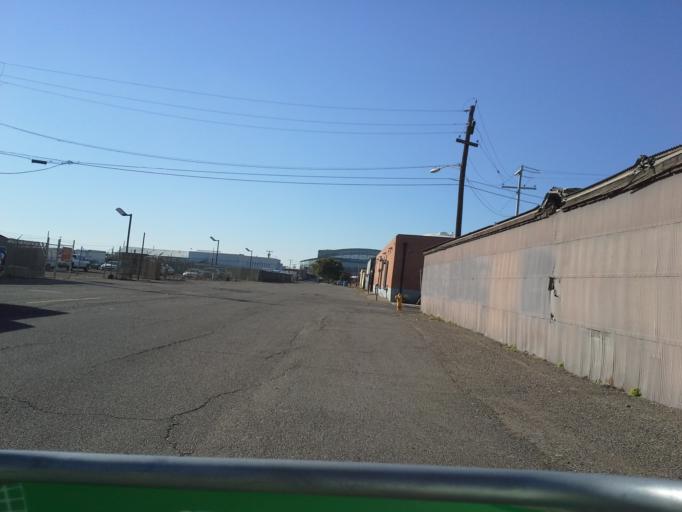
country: US
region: Arizona
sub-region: Maricopa County
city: Phoenix
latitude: 33.4452
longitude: -112.0538
